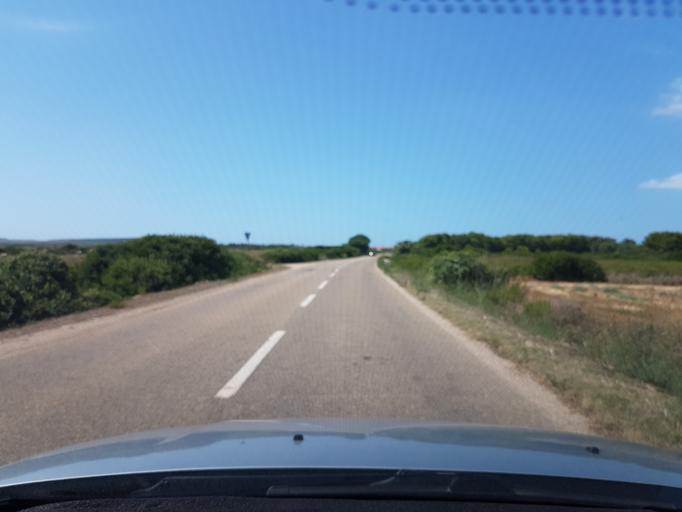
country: IT
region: Sardinia
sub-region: Provincia di Oristano
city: Riola Sardo
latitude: 40.0340
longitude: 8.4237
